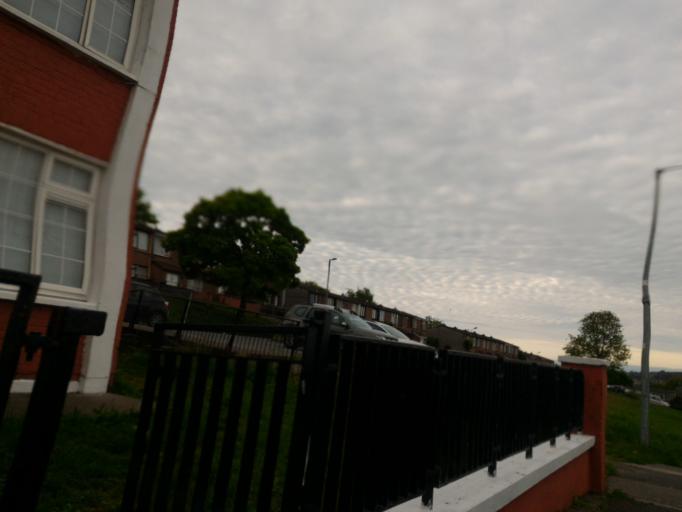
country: IE
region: Munster
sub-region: County Cork
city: Cork
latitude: 51.9128
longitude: -8.4647
